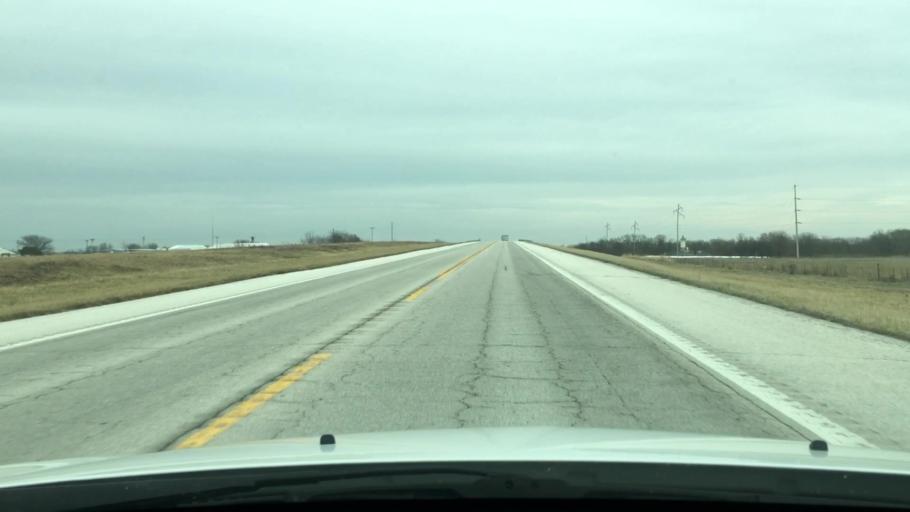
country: US
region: Missouri
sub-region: Pike County
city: Bowling Green
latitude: 39.3544
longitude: -91.2154
